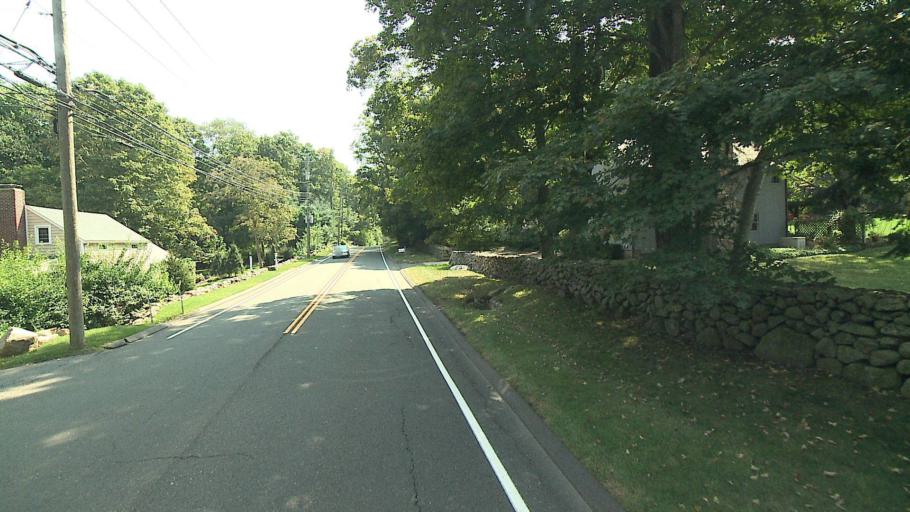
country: US
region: Connecticut
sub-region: Fairfield County
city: Georgetown
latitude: 41.2505
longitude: -73.4179
